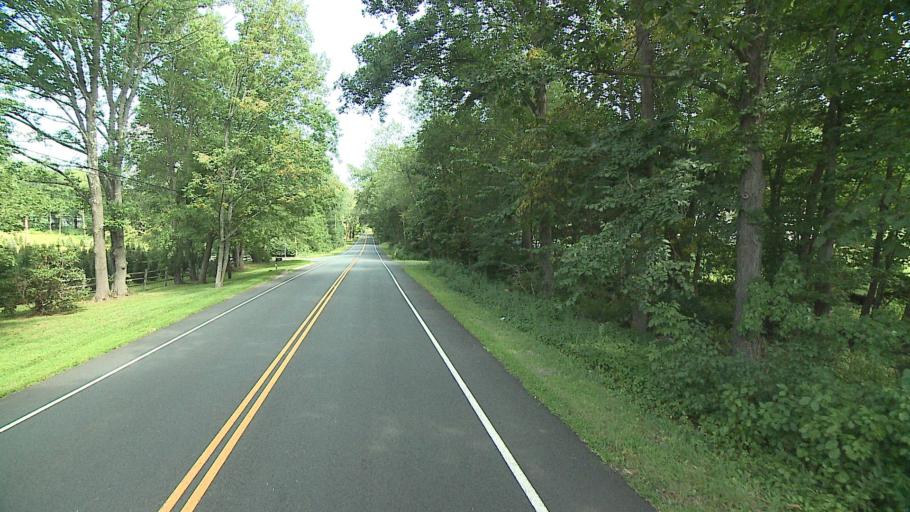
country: US
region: Connecticut
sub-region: Fairfield County
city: Trumbull
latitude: 41.2942
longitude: -73.2887
